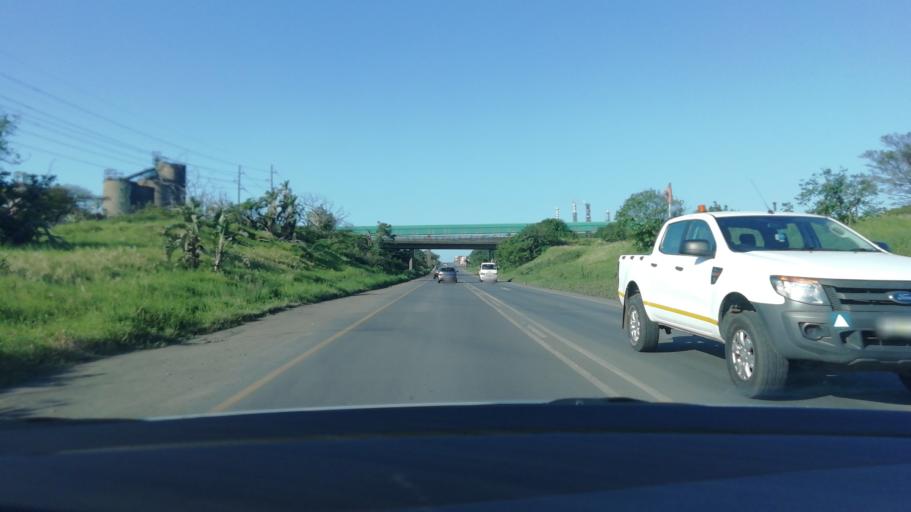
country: ZA
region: KwaZulu-Natal
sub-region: uThungulu District Municipality
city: Richards Bay
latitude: -28.7800
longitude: 32.0290
